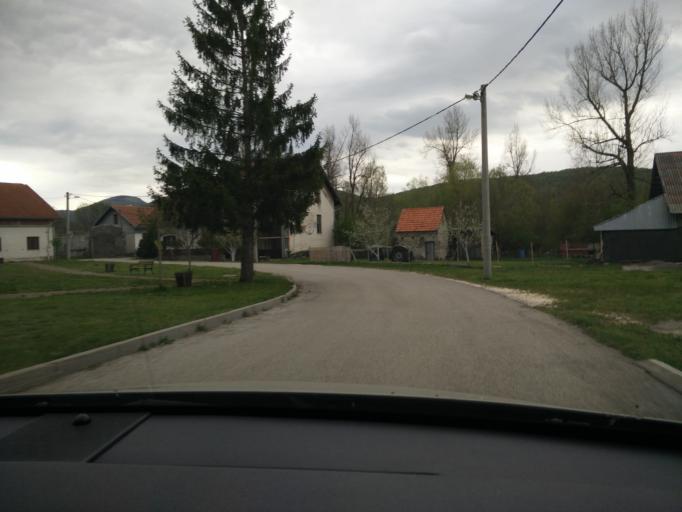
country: HR
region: Zadarska
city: Obrovac
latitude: 44.3904
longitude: 15.6864
